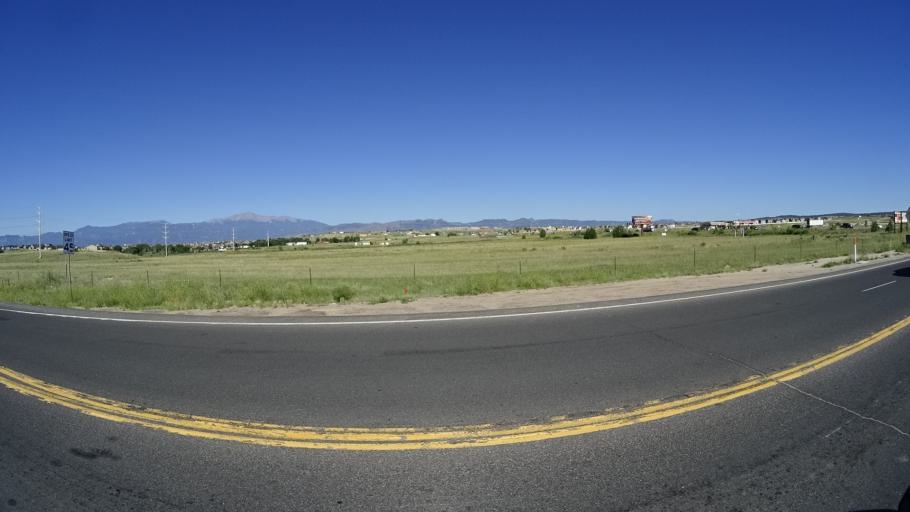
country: US
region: Colorado
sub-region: El Paso County
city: Black Forest
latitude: 38.9395
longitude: -104.6782
